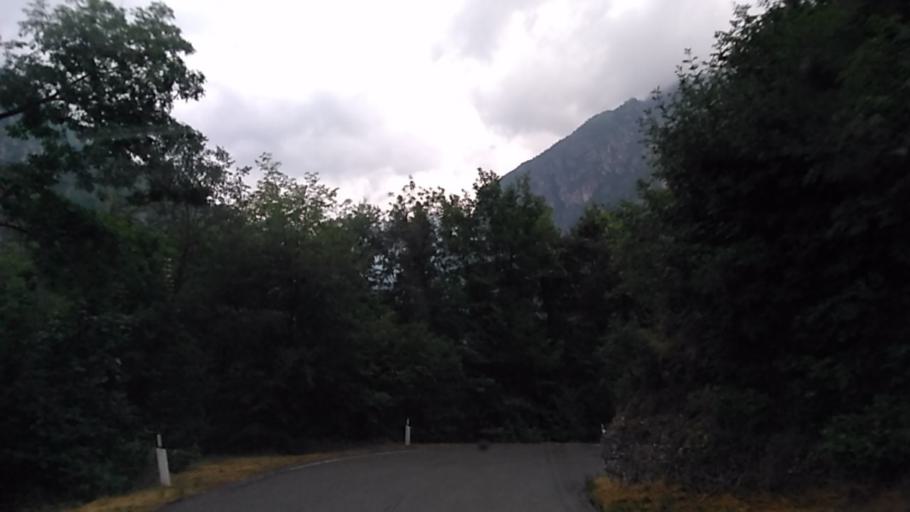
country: IT
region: Lombardy
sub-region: Provincia di Brescia
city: Pieve
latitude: 45.7825
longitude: 10.7208
